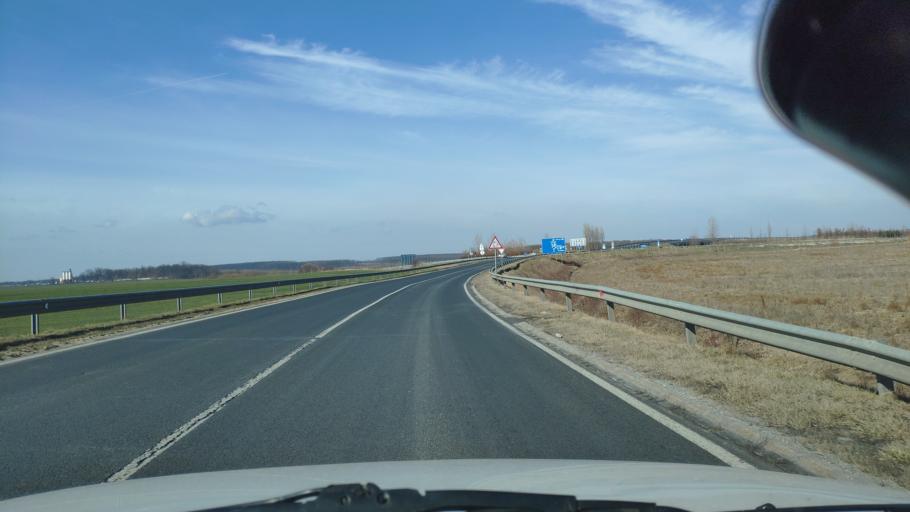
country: HU
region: Zala
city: Nagykanizsa
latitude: 46.4735
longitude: 17.0312
